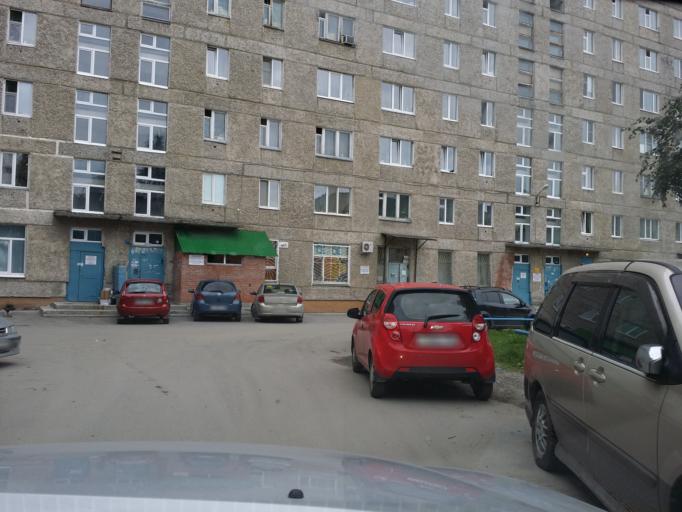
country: RU
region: Khanty-Mansiyskiy Avtonomnyy Okrug
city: Nizhnevartovsk
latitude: 60.9280
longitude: 76.5852
